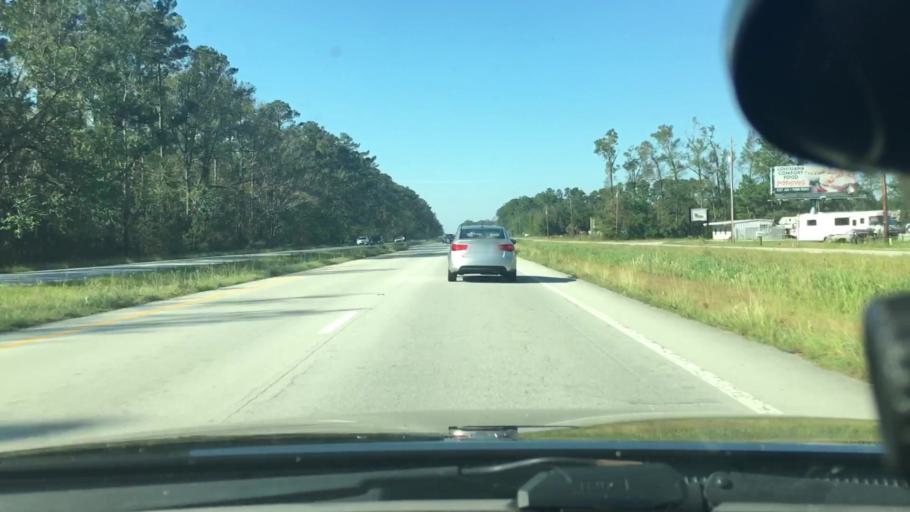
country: US
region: North Carolina
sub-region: Craven County
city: Fairfield Harbour
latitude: 35.0293
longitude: -77.0023
